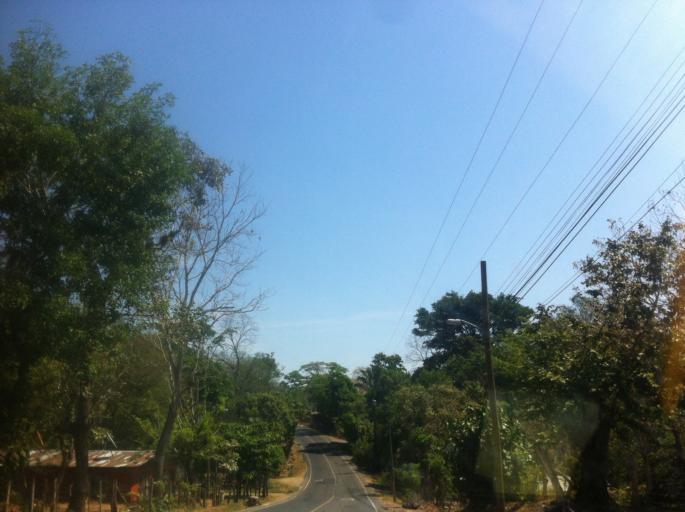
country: CR
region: Guanacaste
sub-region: Canton de Nicoya
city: Nicoya
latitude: 10.1184
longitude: -85.4485
